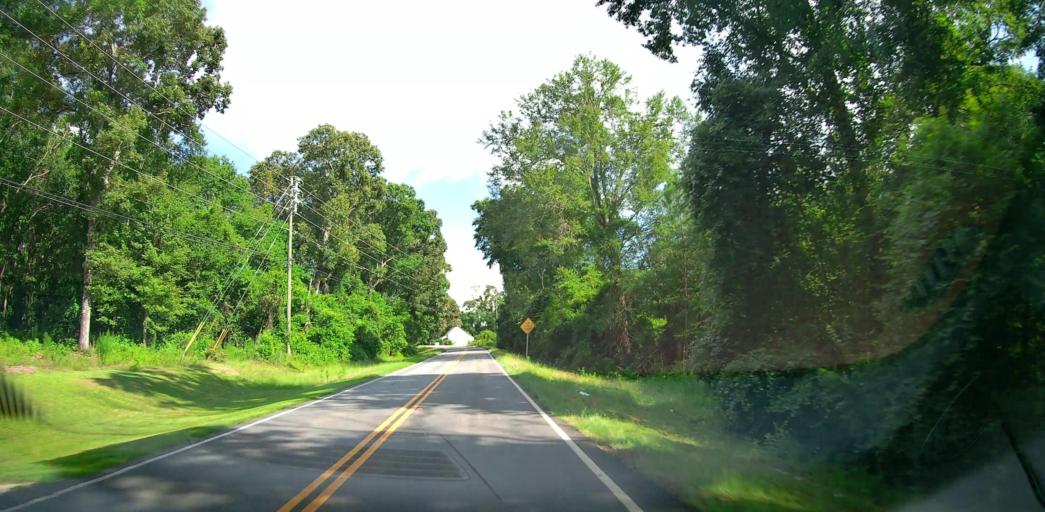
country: US
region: Georgia
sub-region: Houston County
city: Centerville
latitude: 32.5357
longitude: -83.6738
